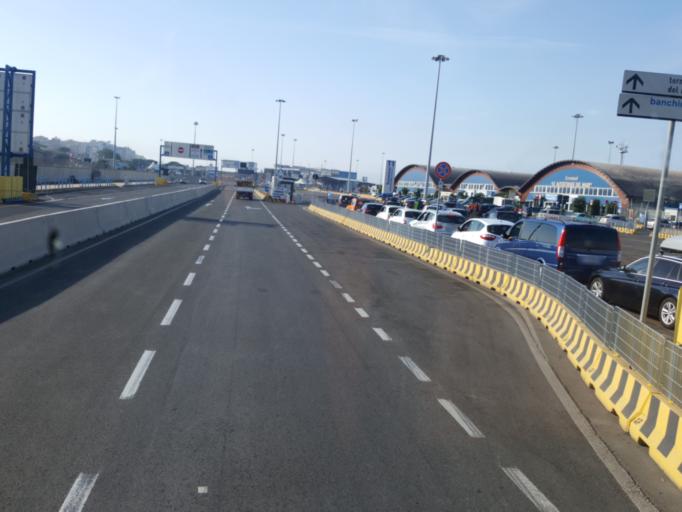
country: IT
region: Latium
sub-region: Citta metropolitana di Roma Capitale
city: Civitavecchia
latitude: 42.1006
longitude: 11.7835
